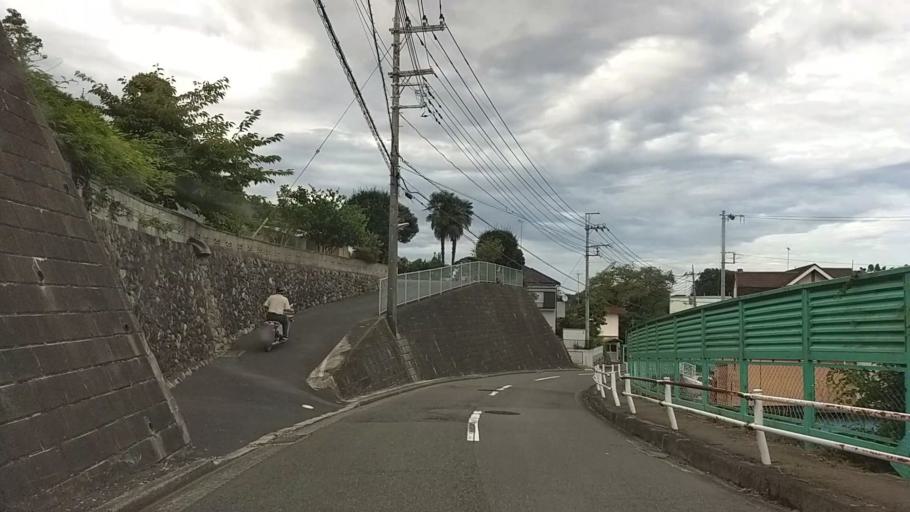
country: JP
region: Tokyo
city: Hachioji
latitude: 35.6297
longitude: 139.2955
